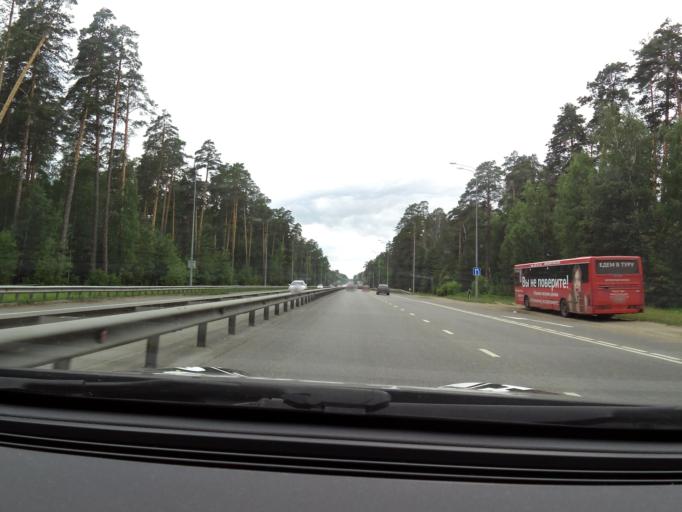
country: RU
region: Tatarstan
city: Staroye Arakchino
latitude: 55.8355
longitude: 48.9771
